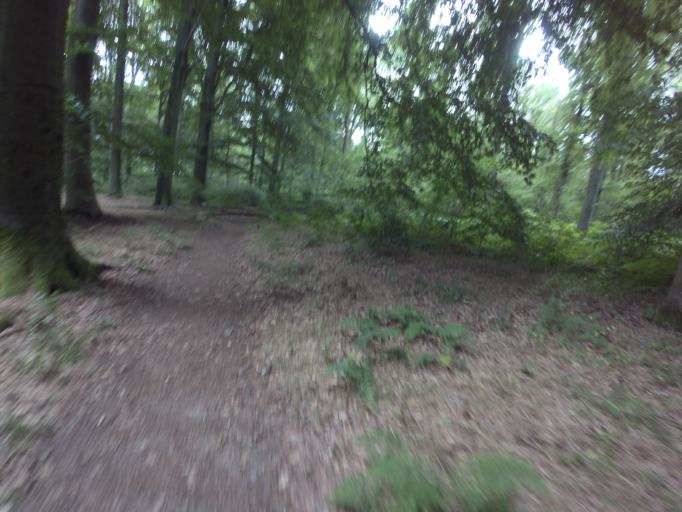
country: BE
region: Wallonia
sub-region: Province de Liege
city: La Calamine
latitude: 50.6998
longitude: 6.0209
